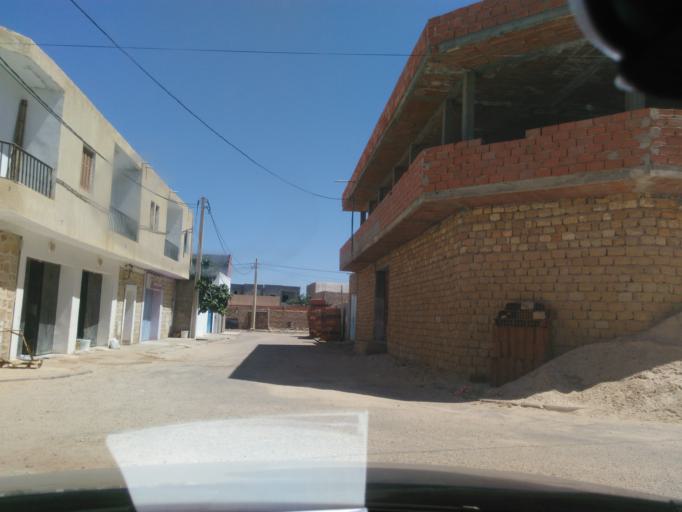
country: TN
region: Tataouine
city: Tataouine
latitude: 32.9493
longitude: 10.4637
